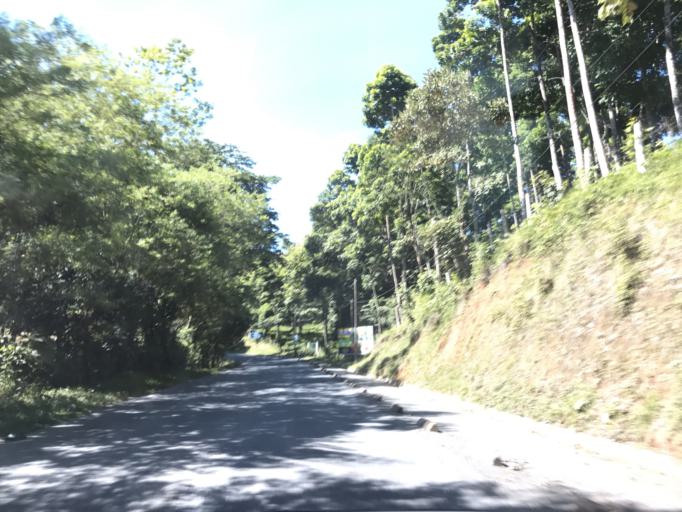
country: GT
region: Izabal
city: Morales
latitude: 15.6514
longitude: -89.0091
